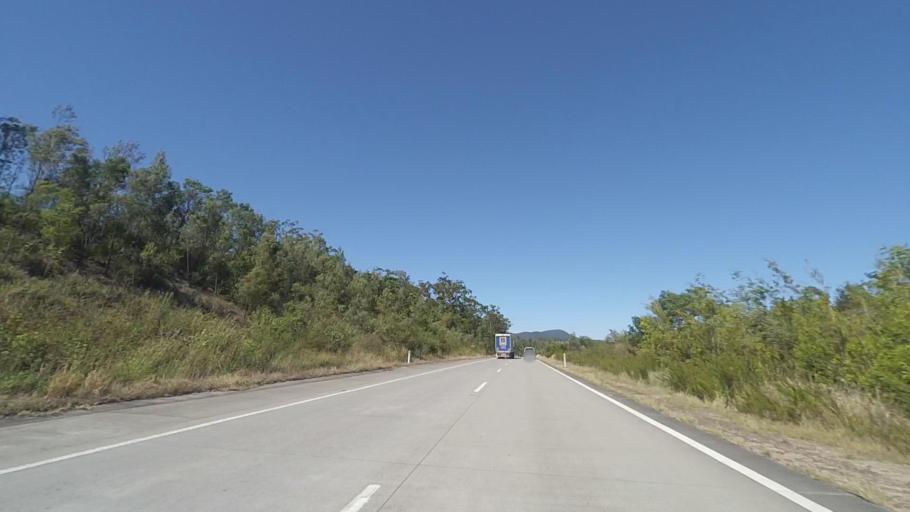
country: AU
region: New South Wales
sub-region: Port Stephens Shire
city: Port Stephens
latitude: -32.6209
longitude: 152.0683
